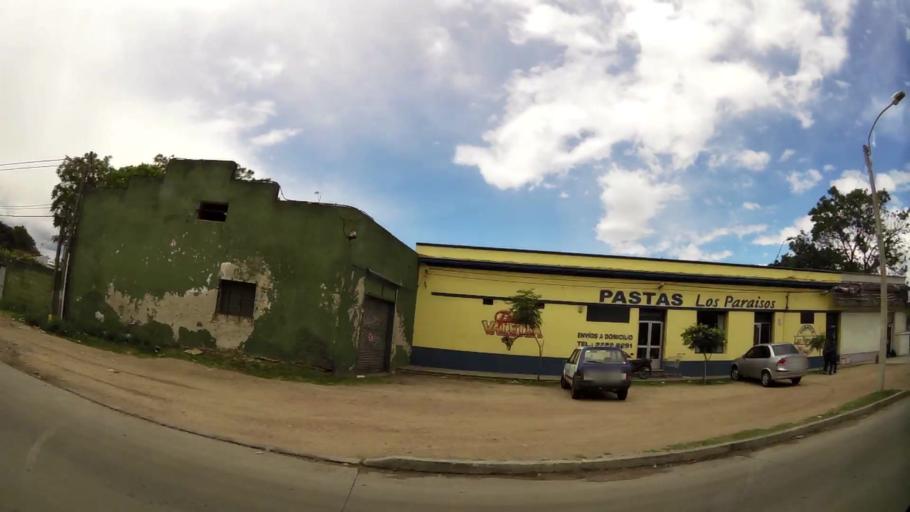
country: UY
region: Canelones
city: La Paz
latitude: -34.8057
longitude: -56.1612
